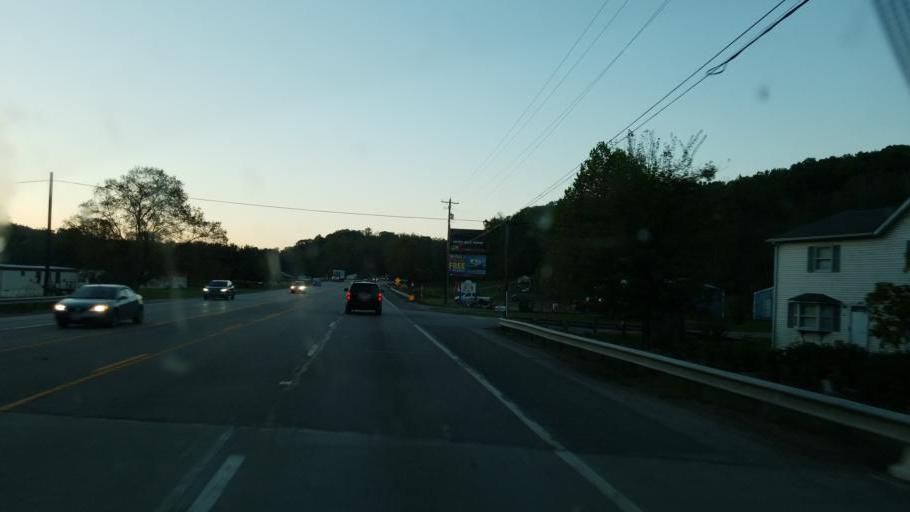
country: US
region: Ohio
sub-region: Pike County
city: Waverly
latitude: 39.1840
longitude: -82.9756
